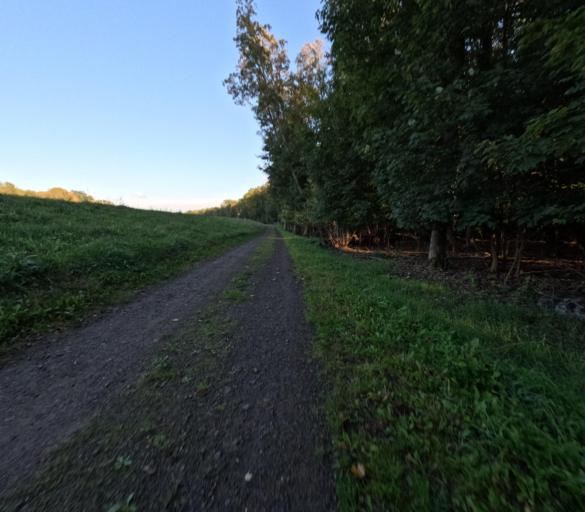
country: DE
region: Saxony
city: Schkeuditz
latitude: 51.3711
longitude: 12.2866
